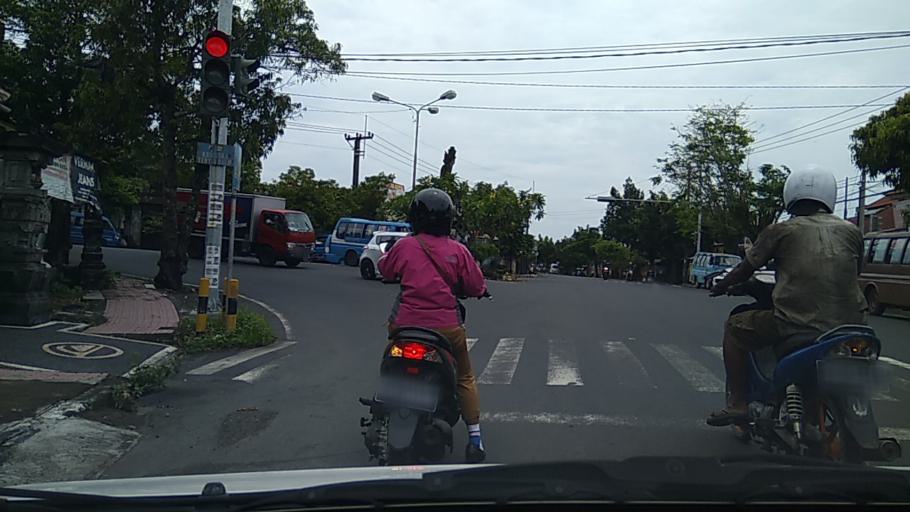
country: ID
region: Bali
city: Banjar Kelodan
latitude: -8.5411
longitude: 115.3472
